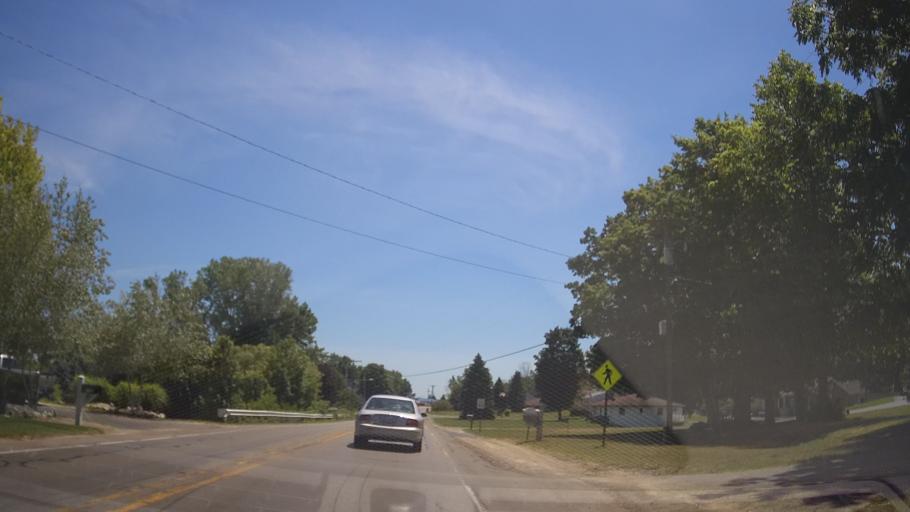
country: US
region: Michigan
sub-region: Grand Traverse County
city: Traverse City
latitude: 44.7050
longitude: -85.6922
